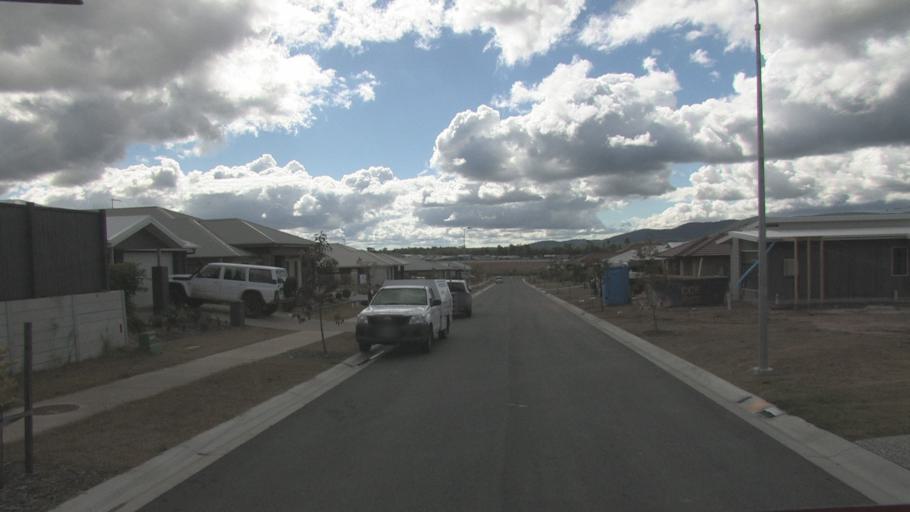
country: AU
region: Queensland
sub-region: Logan
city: Chambers Flat
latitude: -27.8120
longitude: 153.1154
